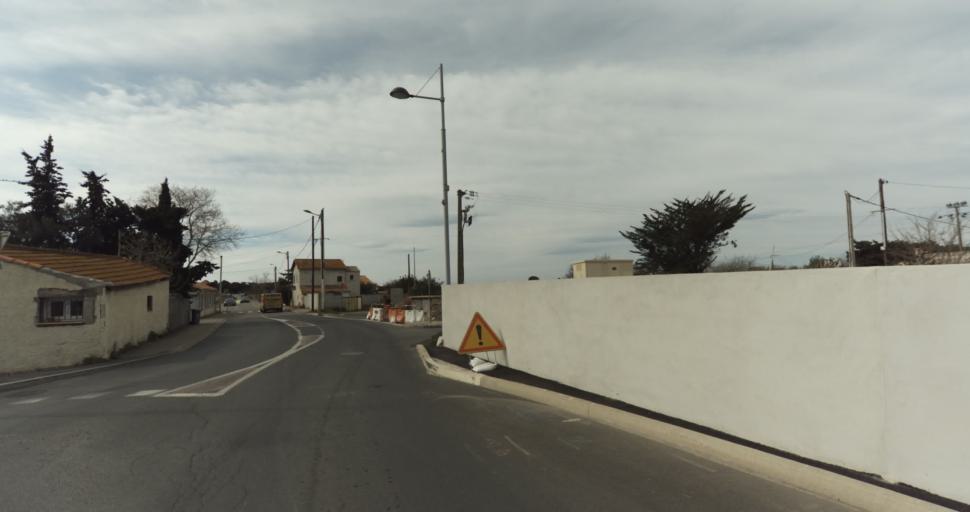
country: FR
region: Languedoc-Roussillon
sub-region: Departement de l'Herault
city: Marseillan
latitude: 43.3204
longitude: 3.5362
